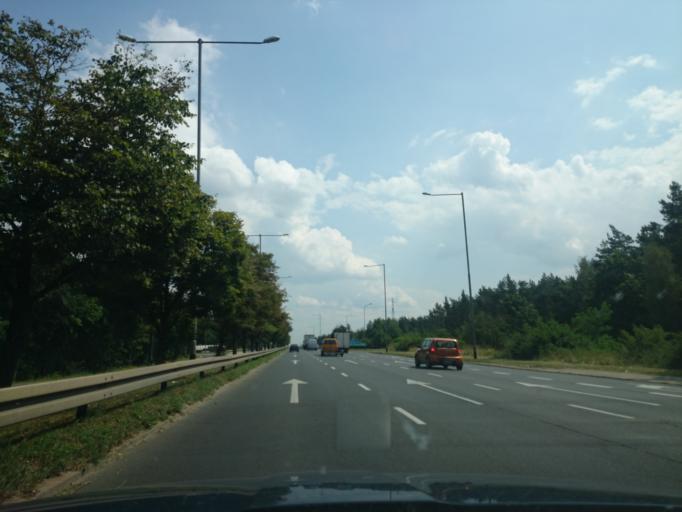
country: PL
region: West Pomeranian Voivodeship
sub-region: Powiat gryfinski
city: Stare Czarnowo
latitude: 53.3752
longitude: 14.6979
